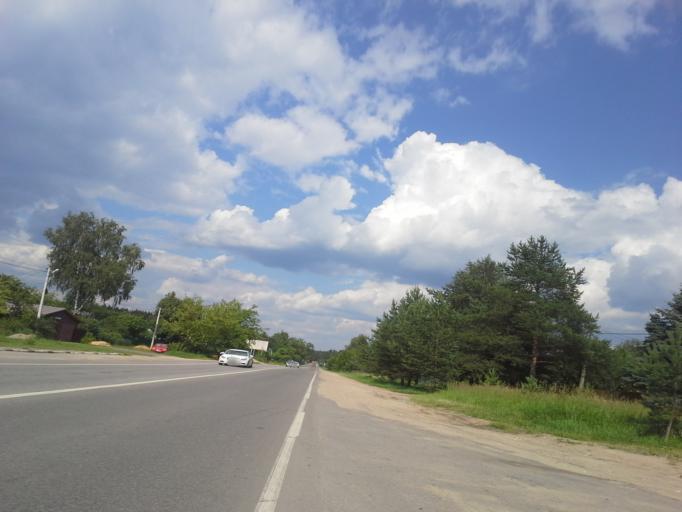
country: RU
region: Moskovskaya
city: Naro-Fominsk
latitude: 55.3965
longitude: 36.7717
